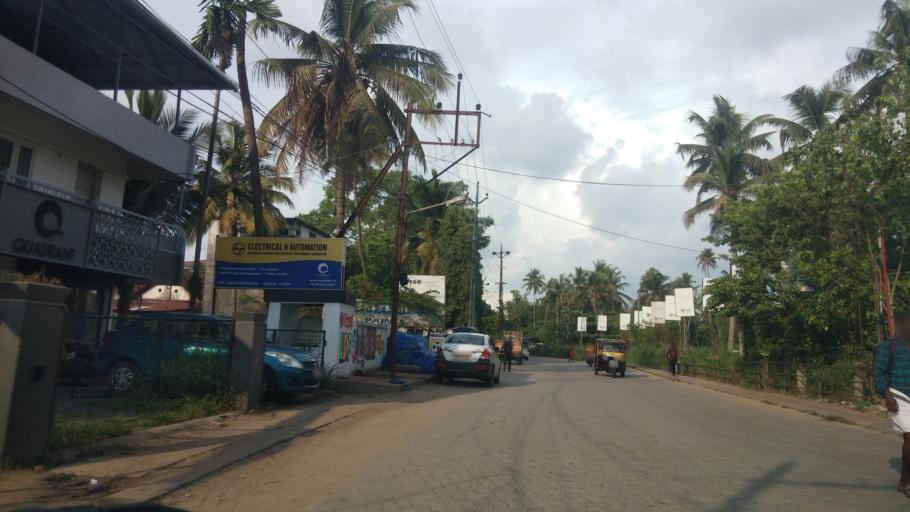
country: IN
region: Kerala
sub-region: Ernakulam
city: Cochin
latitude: 9.9690
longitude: 76.3193
